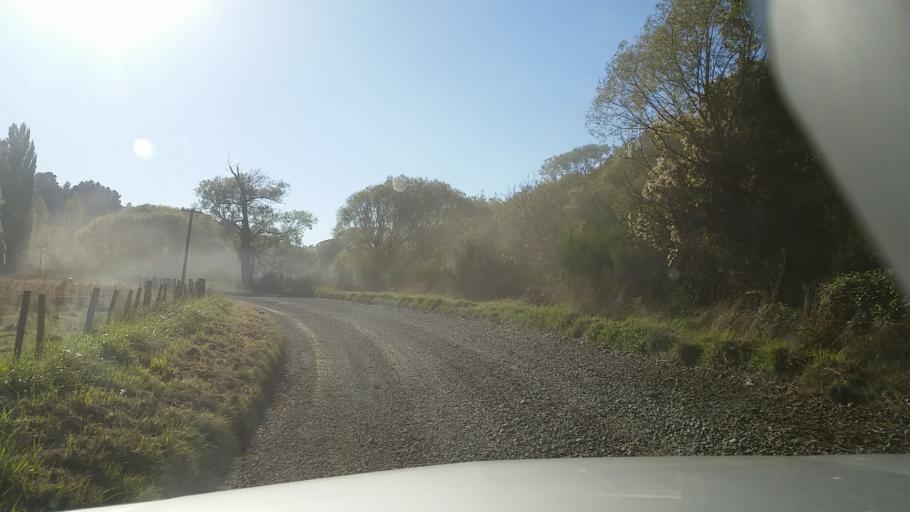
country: NZ
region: Marlborough
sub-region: Marlborough District
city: Blenheim
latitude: -41.4499
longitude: 173.8751
